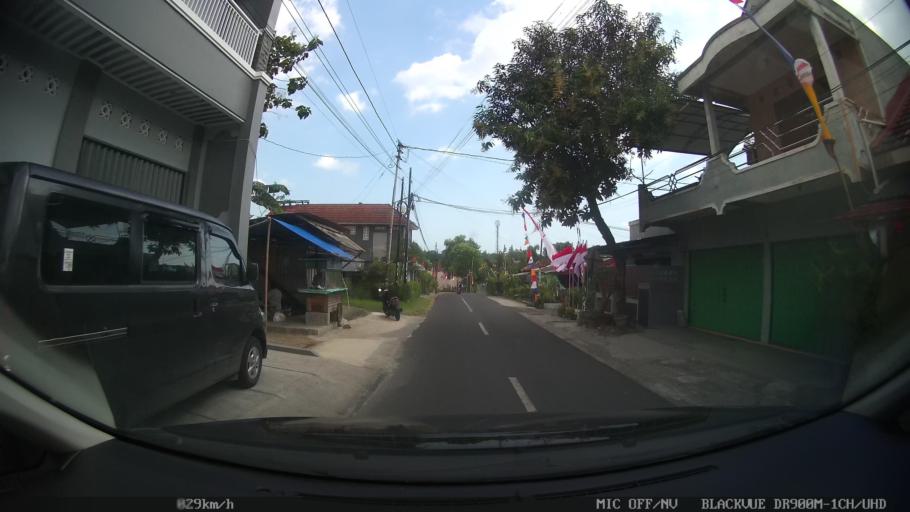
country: ID
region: Daerah Istimewa Yogyakarta
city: Gamping Lor
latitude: -7.7892
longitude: 110.3417
